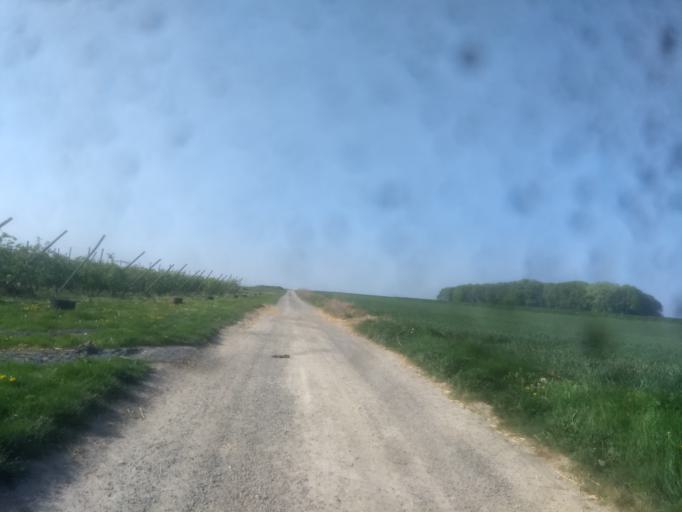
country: FR
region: Nord-Pas-de-Calais
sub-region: Departement du Pas-de-Calais
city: Beaurains
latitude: 50.2623
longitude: 2.8067
